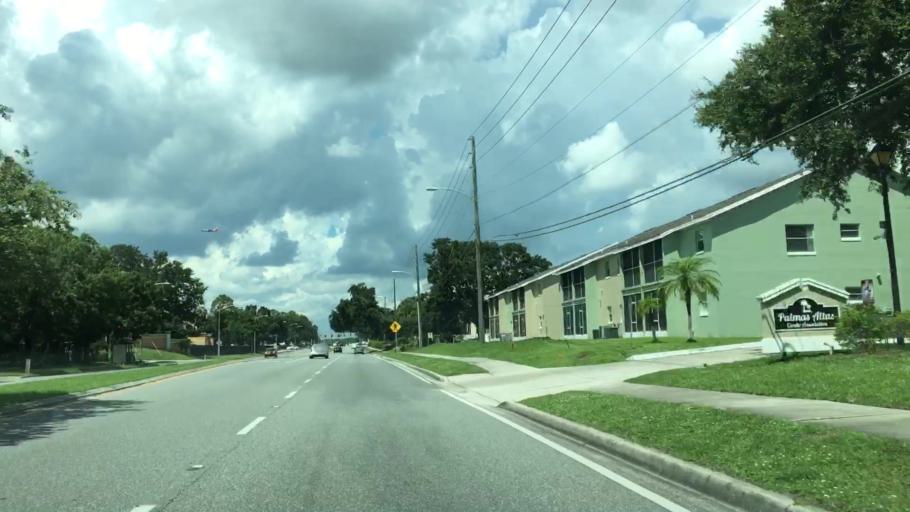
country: US
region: Florida
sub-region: Orange County
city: Conway
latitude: 28.4990
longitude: -81.3051
